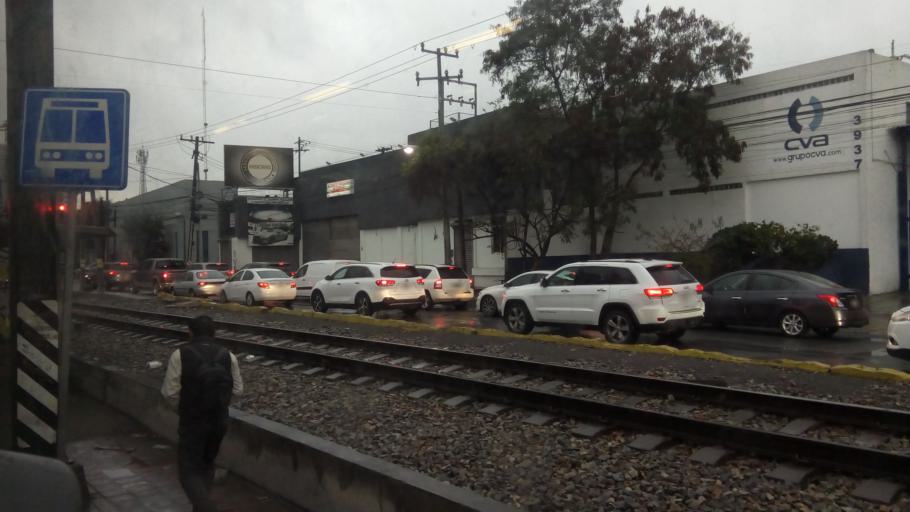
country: MX
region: Nuevo Leon
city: Garza Garcia
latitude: 25.6721
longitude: -100.3732
